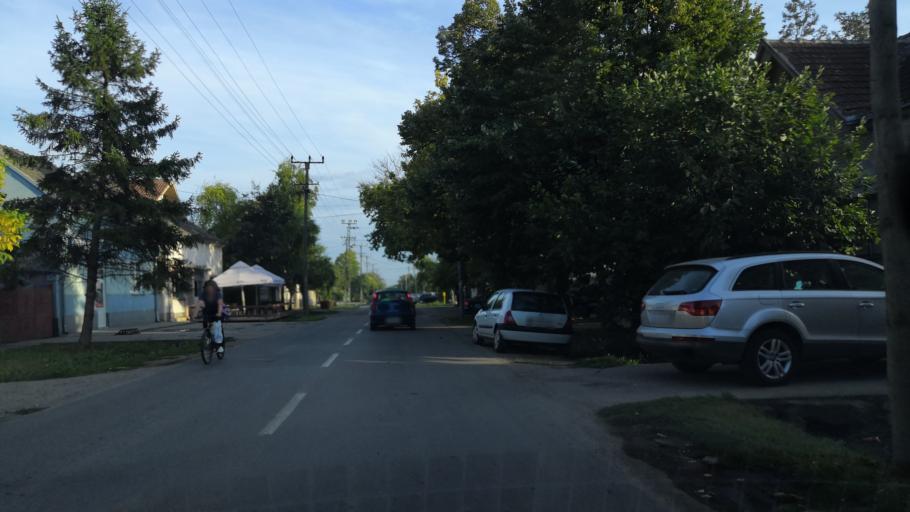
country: RS
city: Novi Karlovci
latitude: 45.0776
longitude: 20.1796
